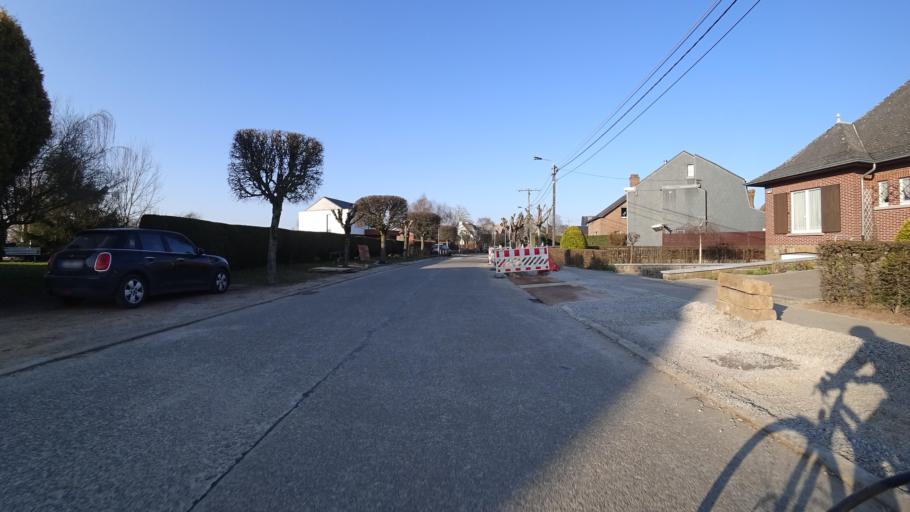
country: BE
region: Wallonia
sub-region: Province de Namur
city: Gembloux
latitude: 50.5654
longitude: 4.6790
